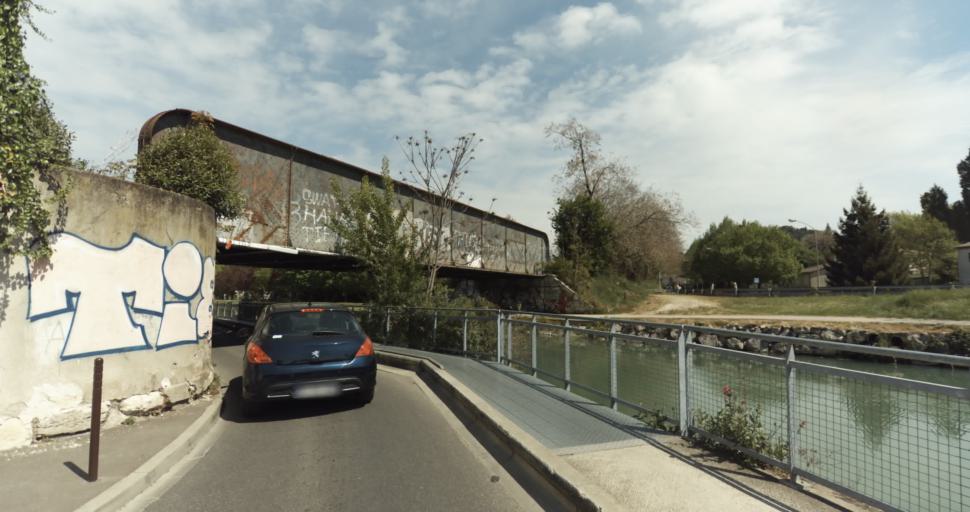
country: FR
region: Aquitaine
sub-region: Departement du Lot-et-Garonne
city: Agen
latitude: 44.2053
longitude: 0.6427
